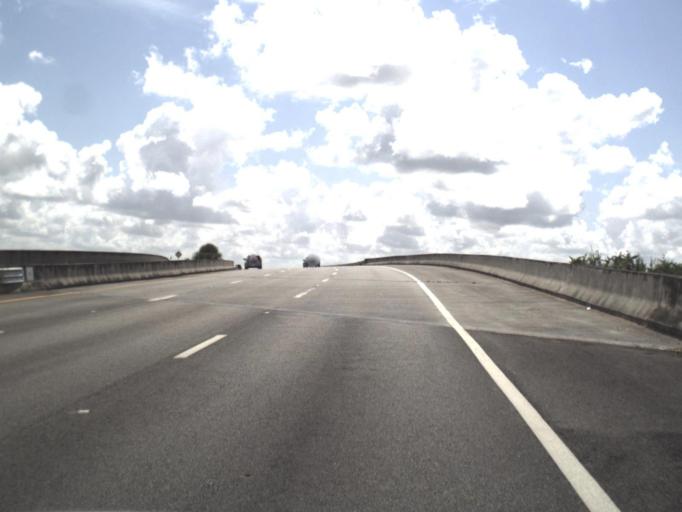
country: US
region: Florida
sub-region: Charlotte County
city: Punta Gorda
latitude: 26.9396
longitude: -82.0284
